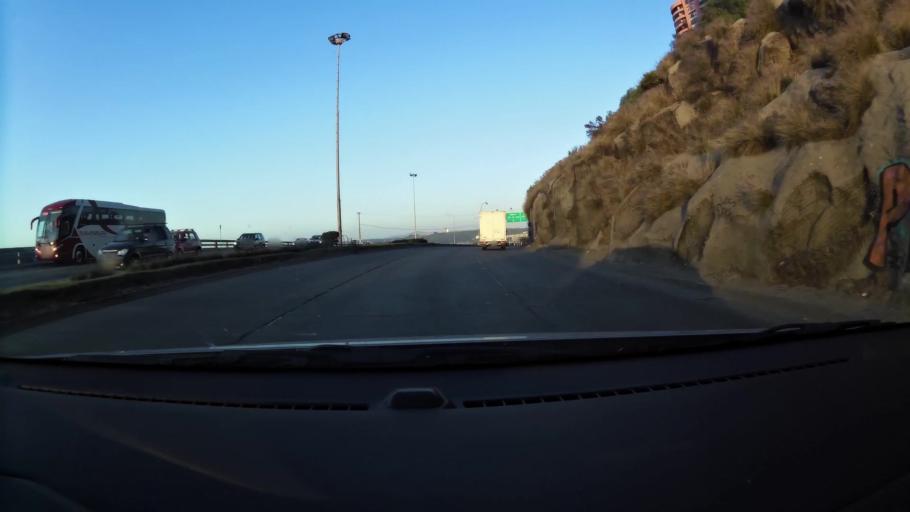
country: CL
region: Valparaiso
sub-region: Provincia de Valparaiso
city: Vina del Mar
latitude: -33.0266
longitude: -71.5852
